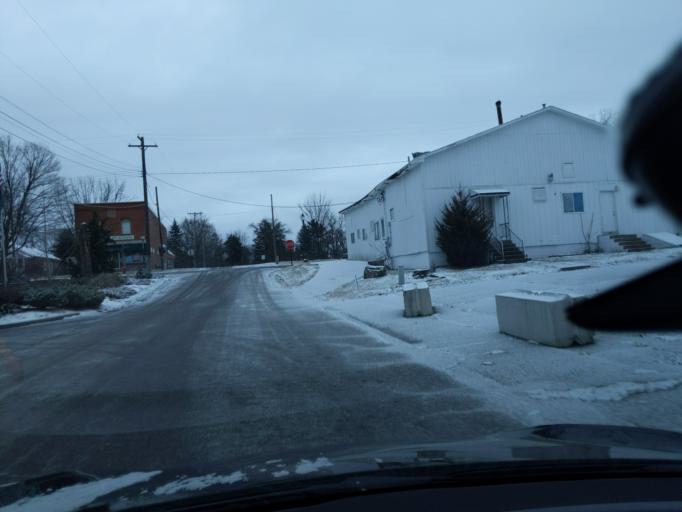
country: US
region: Michigan
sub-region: Ingham County
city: Okemos
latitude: 42.7168
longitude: -84.4306
